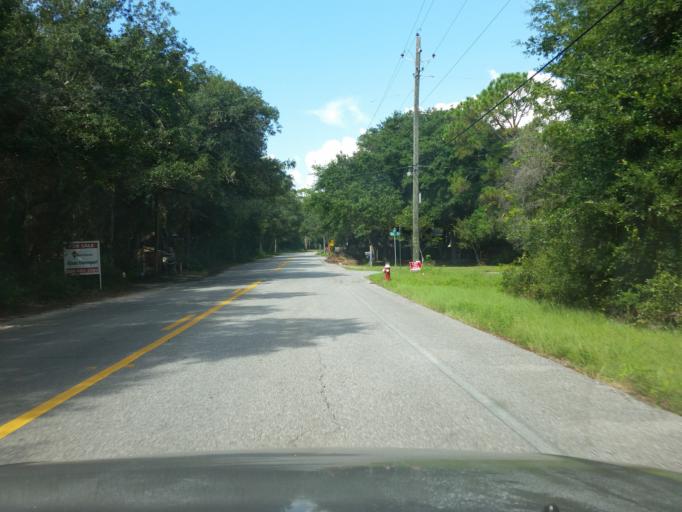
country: US
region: Alabama
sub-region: Baldwin County
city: Orange Beach
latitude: 30.3135
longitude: -87.4543
